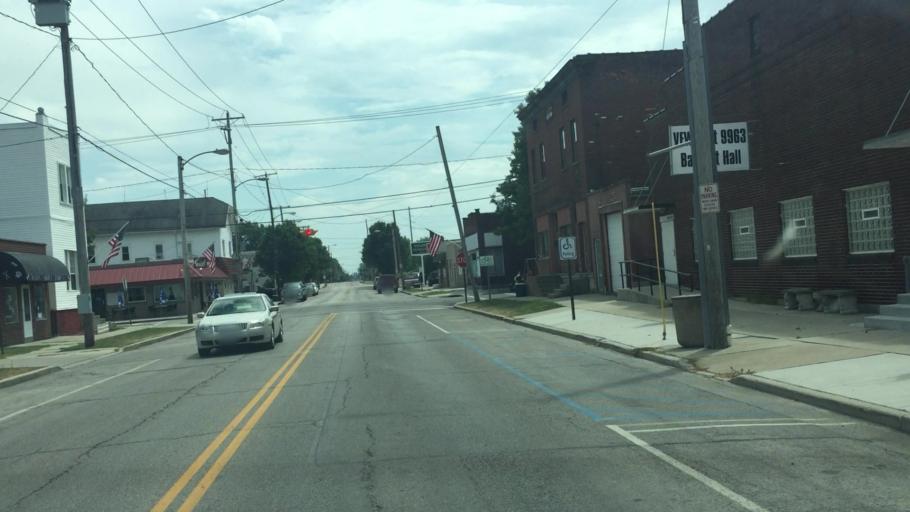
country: US
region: Ohio
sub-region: Wood County
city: Walbridge
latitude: 41.5883
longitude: -83.4934
